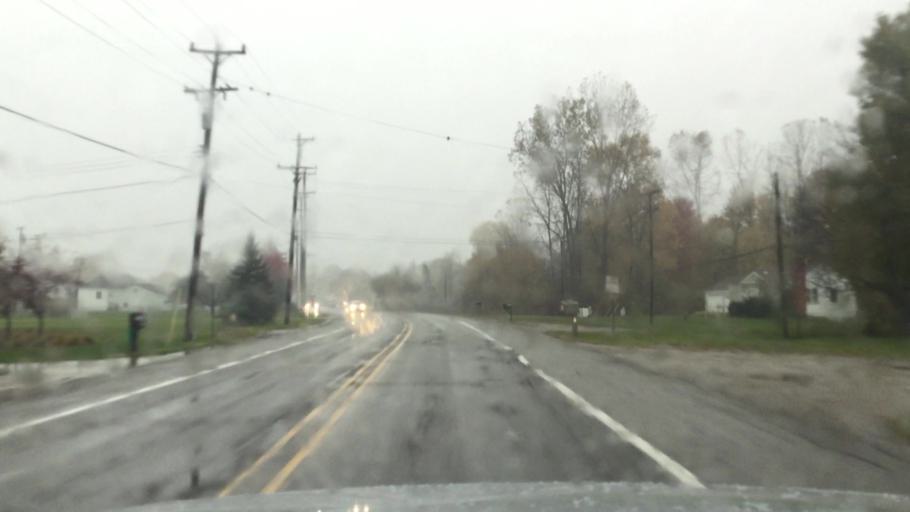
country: US
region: Michigan
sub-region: Macomb County
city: New Baltimore
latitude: 42.6905
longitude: -82.6827
